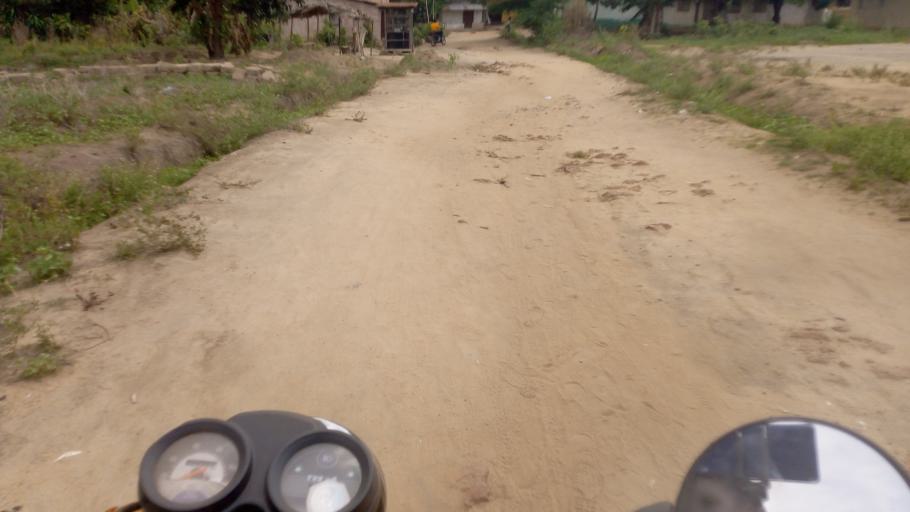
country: SL
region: Western Area
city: Waterloo
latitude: 8.3119
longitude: -13.0632
